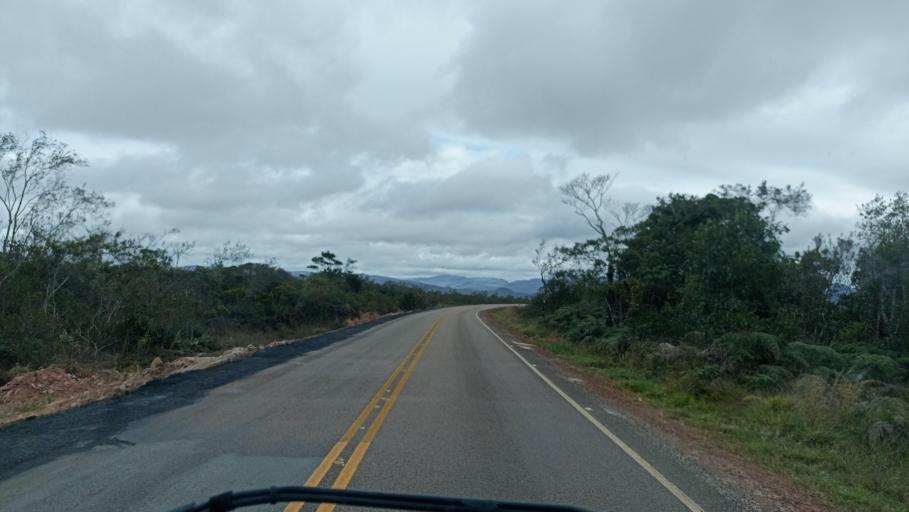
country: BR
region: Bahia
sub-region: Andarai
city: Vera Cruz
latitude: -12.9598
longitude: -41.3210
